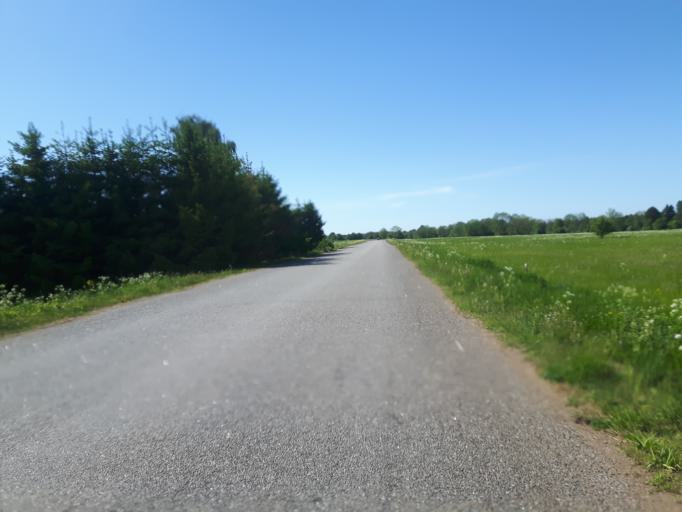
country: EE
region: Laeaene-Virumaa
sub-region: Haljala vald
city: Haljala
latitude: 59.5432
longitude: 26.2186
